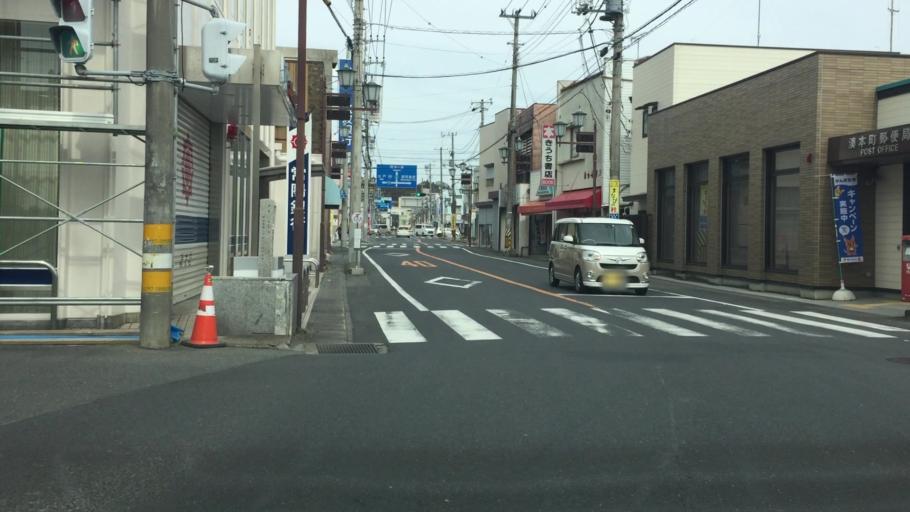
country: JP
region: Ibaraki
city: Oarai
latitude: 36.3410
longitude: 140.5925
